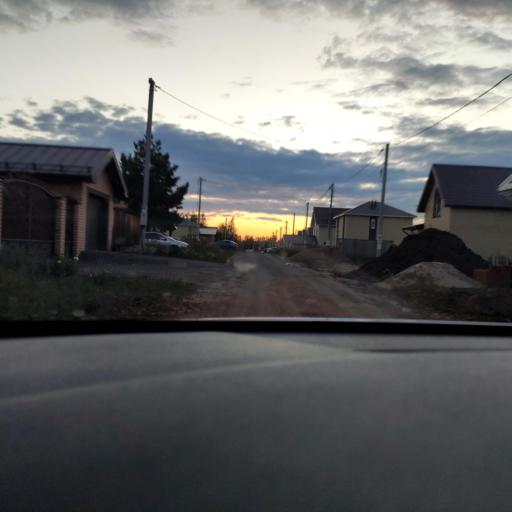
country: RU
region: Tatarstan
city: Stolbishchi
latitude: 55.7221
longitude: 49.3064
